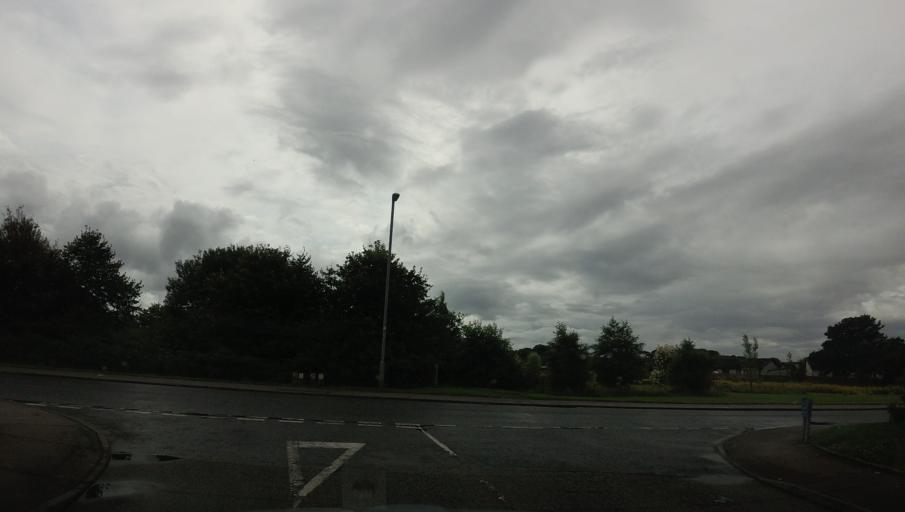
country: GB
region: Scotland
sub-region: Aberdeenshire
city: Stonehaven
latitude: 56.9726
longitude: -2.2310
